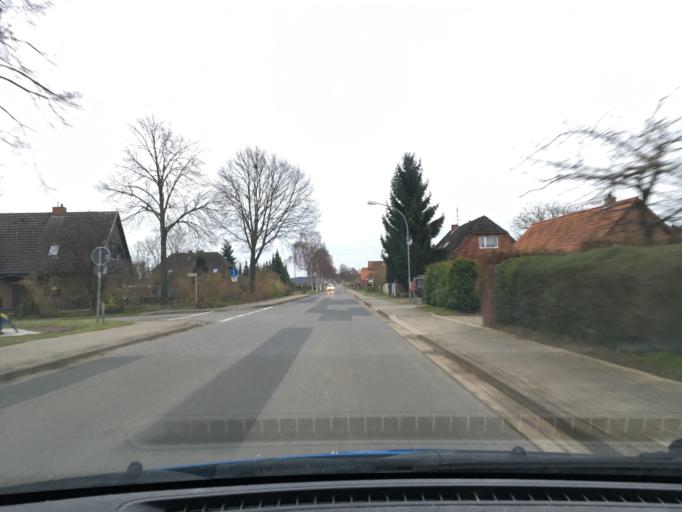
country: DE
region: Lower Saxony
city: Neu Darchau
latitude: 53.2386
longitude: 10.8508
